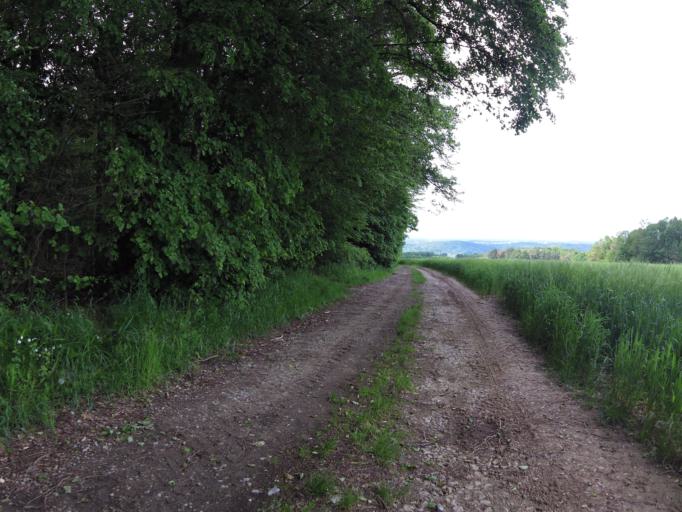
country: DE
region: Bavaria
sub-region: Regierungsbezirk Unterfranken
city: Sommerhausen
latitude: 49.7171
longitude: 10.0308
